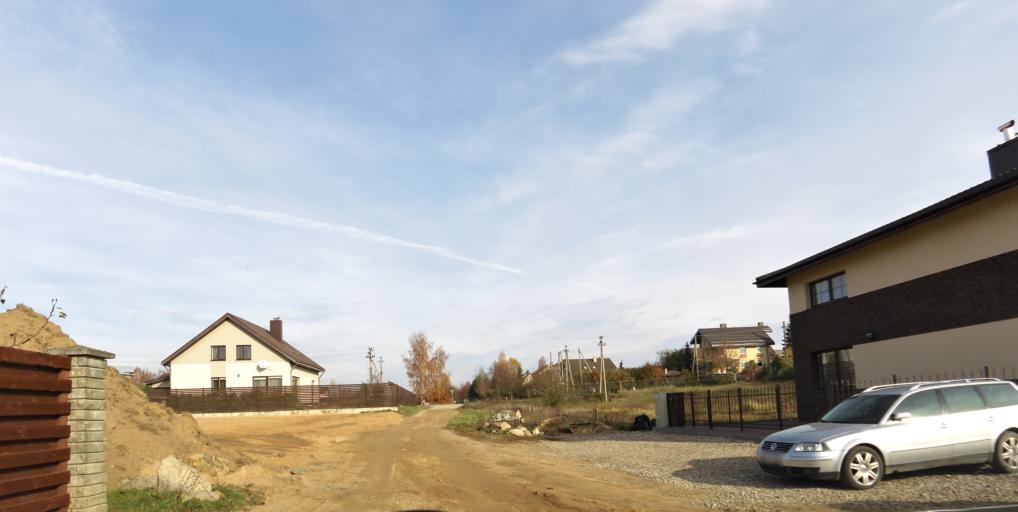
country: LT
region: Vilnius County
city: Pilaite
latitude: 54.7264
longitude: 25.1694
